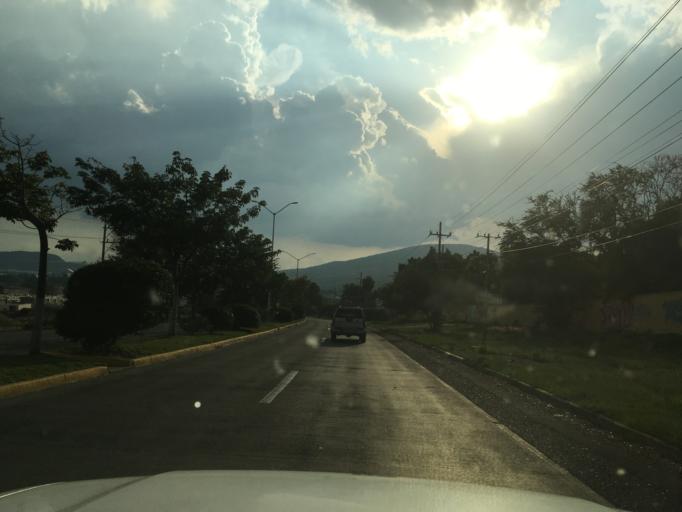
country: MX
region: Jalisco
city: Tlajomulco de Zuniga
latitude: 20.4907
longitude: -103.4729
